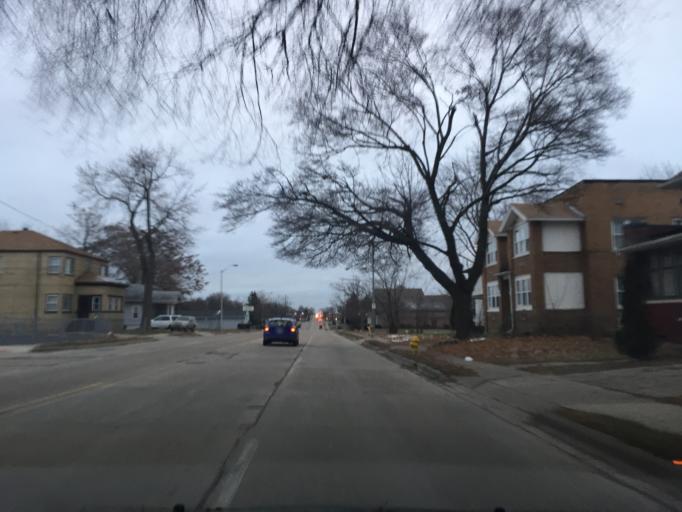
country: US
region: Michigan
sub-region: Oakland County
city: Pontiac
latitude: 42.6344
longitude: -83.2813
